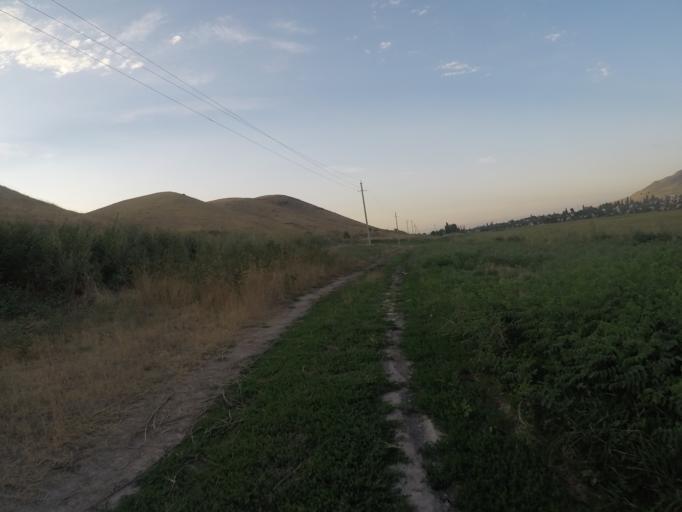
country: KG
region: Chuy
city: Bishkek
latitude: 42.7601
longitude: 74.6361
